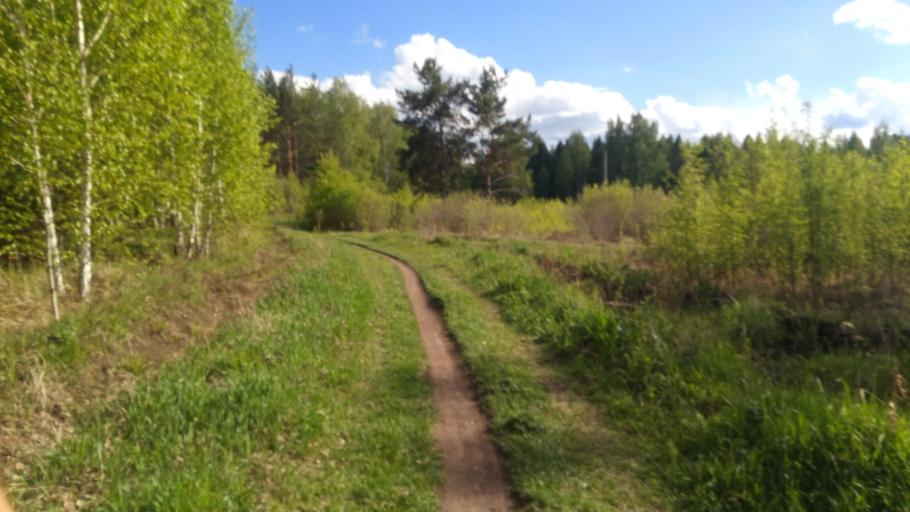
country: RU
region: Chelyabinsk
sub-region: Gorod Chelyabinsk
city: Chelyabinsk
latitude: 55.1650
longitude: 61.3157
